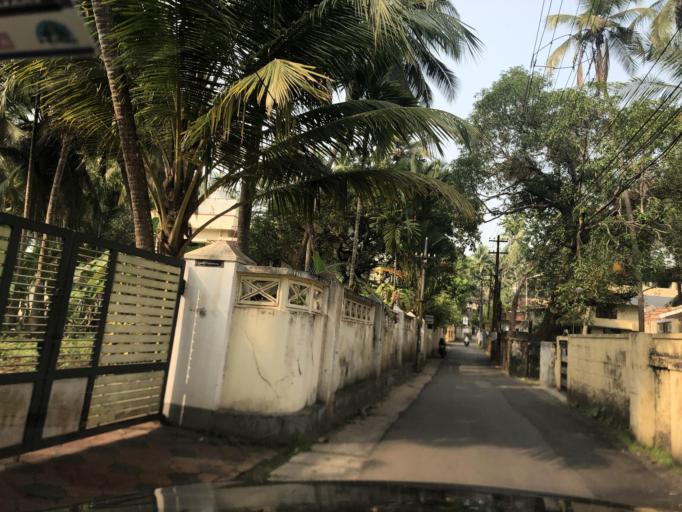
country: IN
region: Kerala
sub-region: Kozhikode
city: Kozhikode
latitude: 11.2771
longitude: 75.7786
